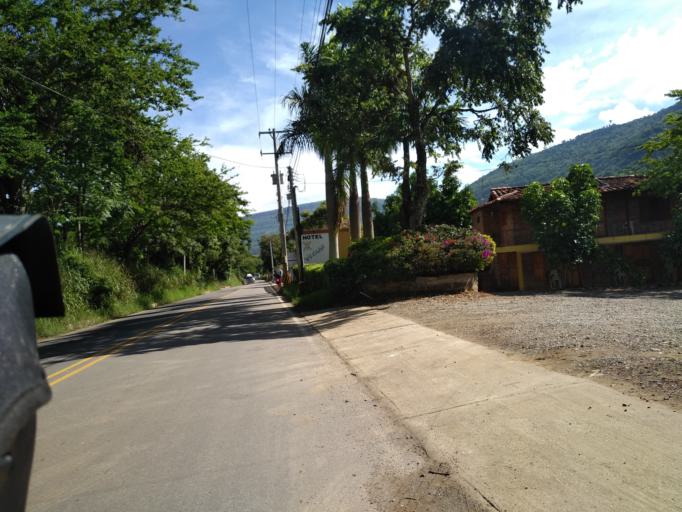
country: CO
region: Santander
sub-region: San Gil
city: San Gil
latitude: 6.5309
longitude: -73.1254
